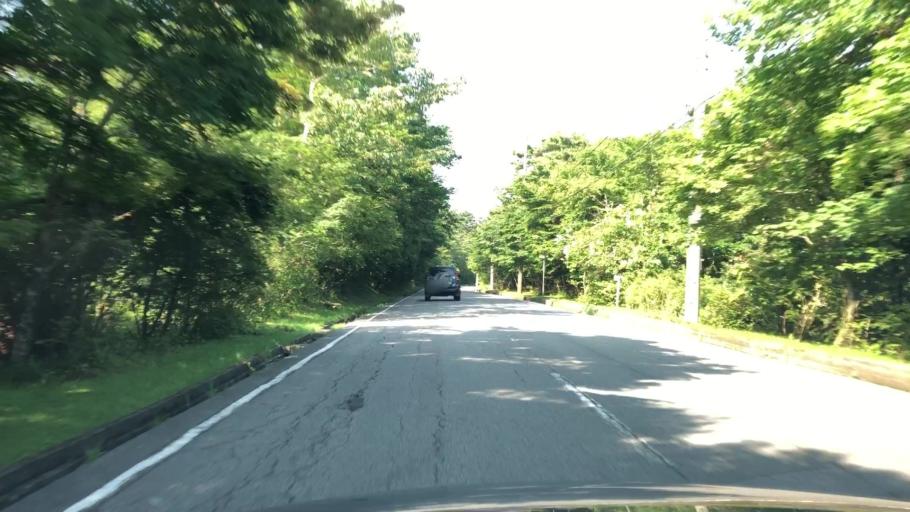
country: JP
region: Shizuoka
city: Gotemba
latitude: 35.3302
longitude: 138.8127
